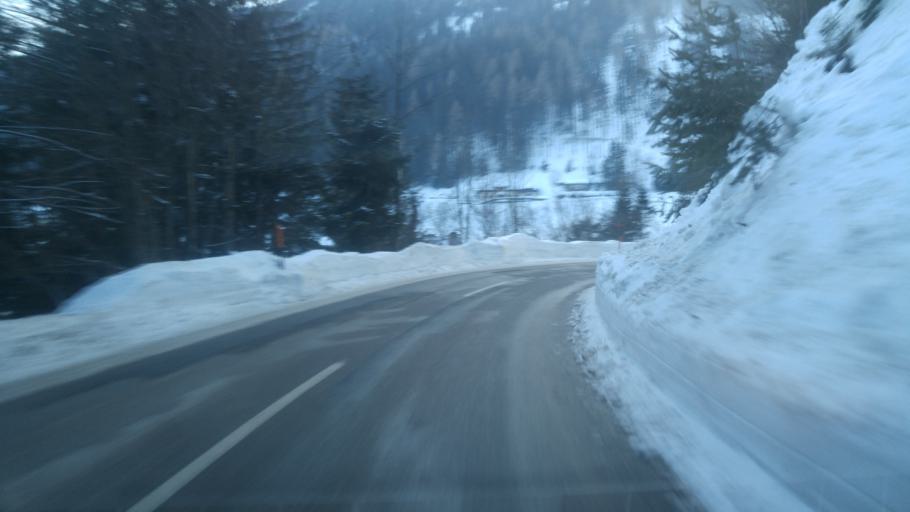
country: AT
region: Lower Austria
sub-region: Politischer Bezirk Wiener Neustadt
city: Rohr im Gebirge
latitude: 47.8896
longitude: 15.6832
